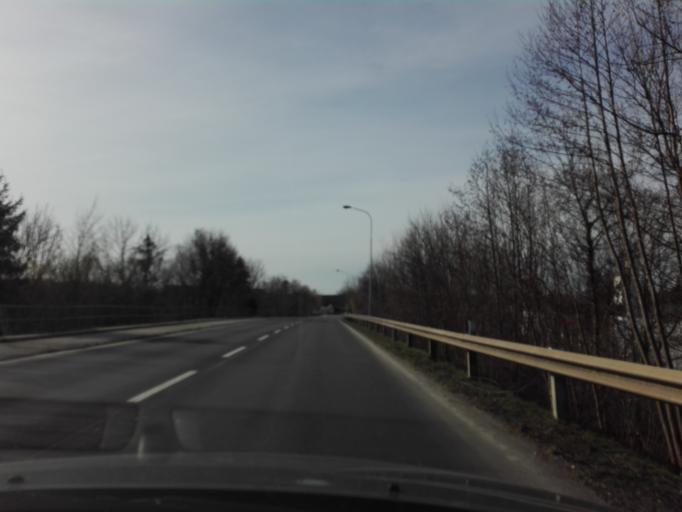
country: AT
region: Upper Austria
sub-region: Politischer Bezirk Linz-Land
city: Ansfelden
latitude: 48.2263
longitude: 14.2986
